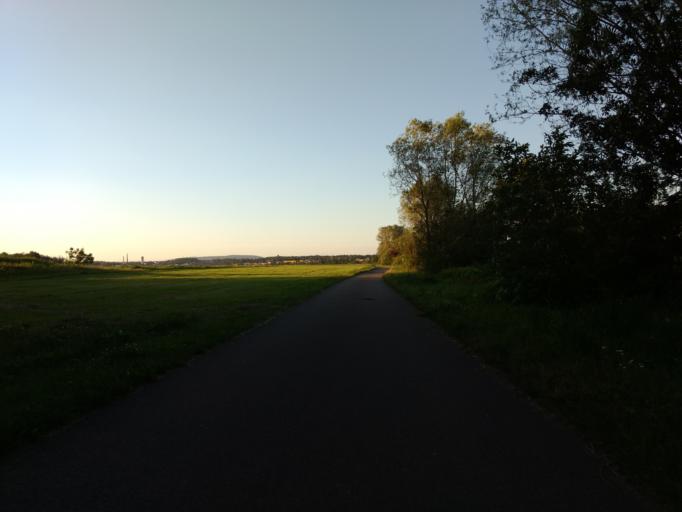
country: DE
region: Saarland
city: Saarlouis
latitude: 49.3073
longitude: 6.7675
